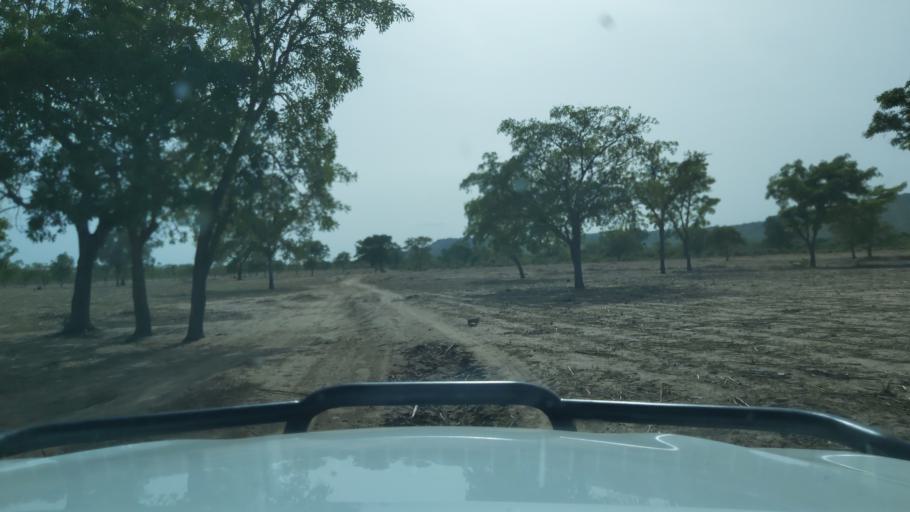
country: ML
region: Koulikoro
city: Koulikoro
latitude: 13.1753
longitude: -7.7461
